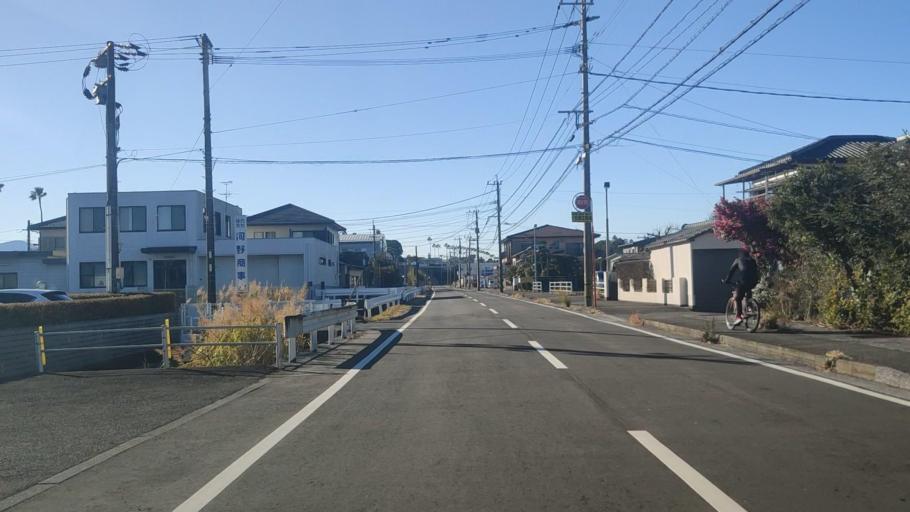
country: JP
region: Miyazaki
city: Miyazaki-shi
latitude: 31.8677
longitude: 131.4365
